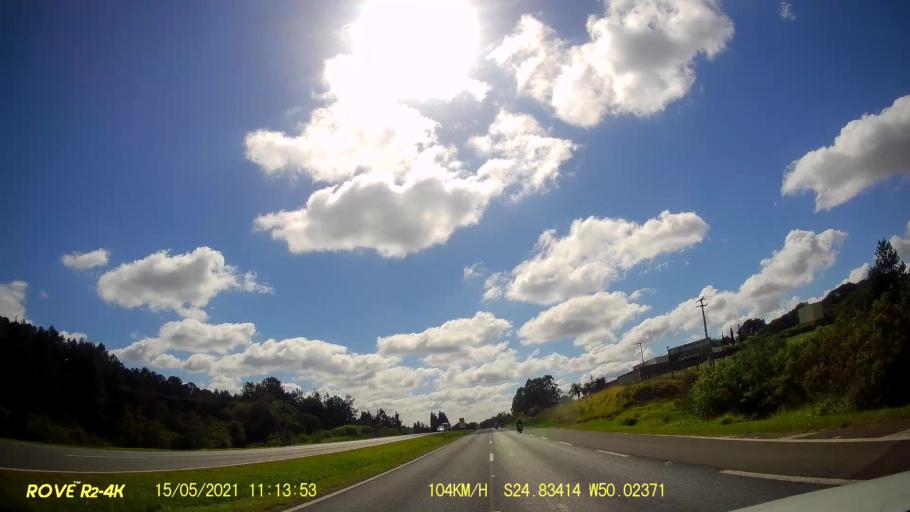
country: BR
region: Parana
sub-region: Castro
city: Castro
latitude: -24.8343
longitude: -50.0239
